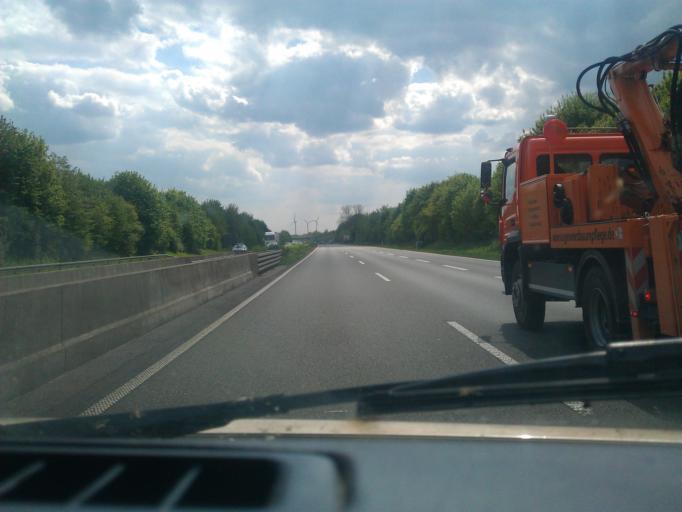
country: DE
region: North Rhine-Westphalia
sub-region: Regierungsbezirk Munster
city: Ochtrup
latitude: 52.2233
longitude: 7.1377
